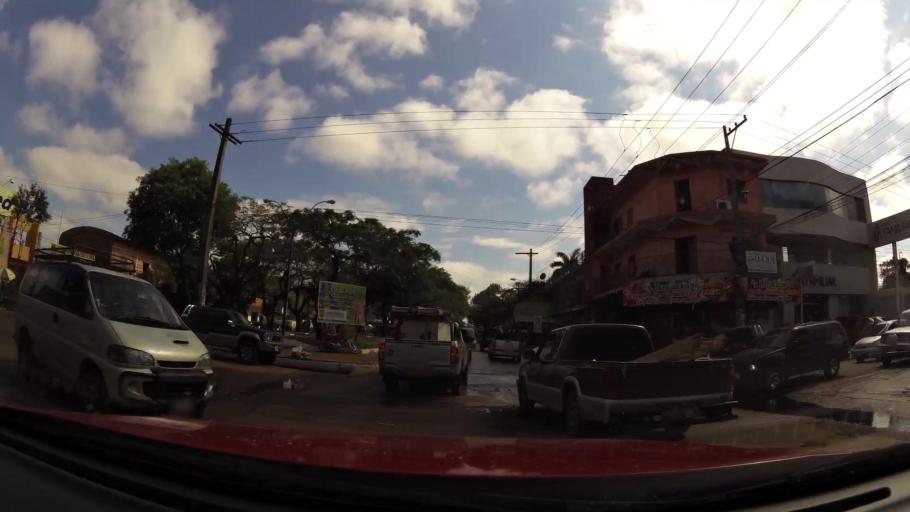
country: PY
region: Central
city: San Lorenzo
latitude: -25.2723
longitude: -57.4865
